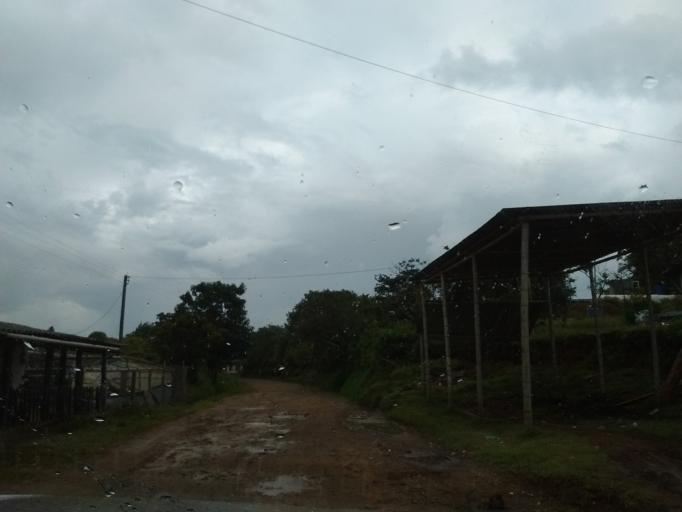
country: CO
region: Cauca
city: Cajibio
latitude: 2.5747
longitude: -76.6517
